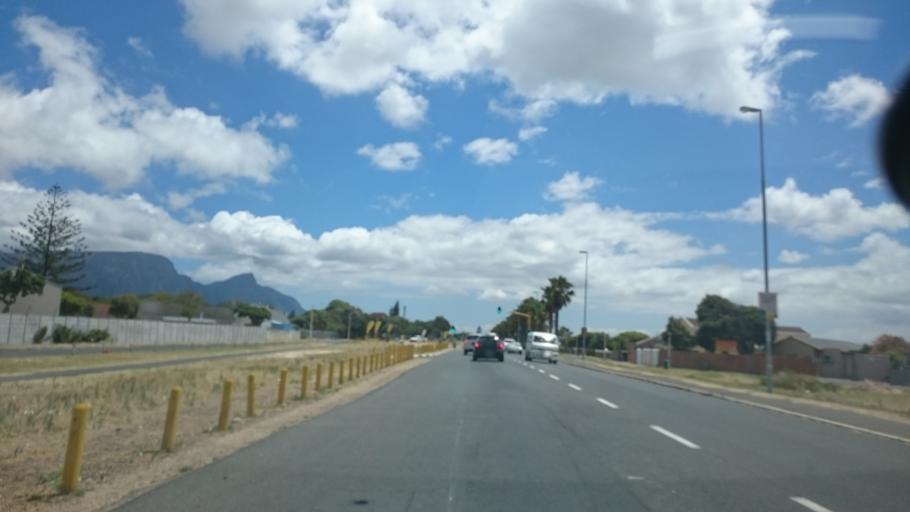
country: ZA
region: Western Cape
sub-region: City of Cape Town
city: Bergvliet
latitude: -34.0577
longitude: 18.4605
